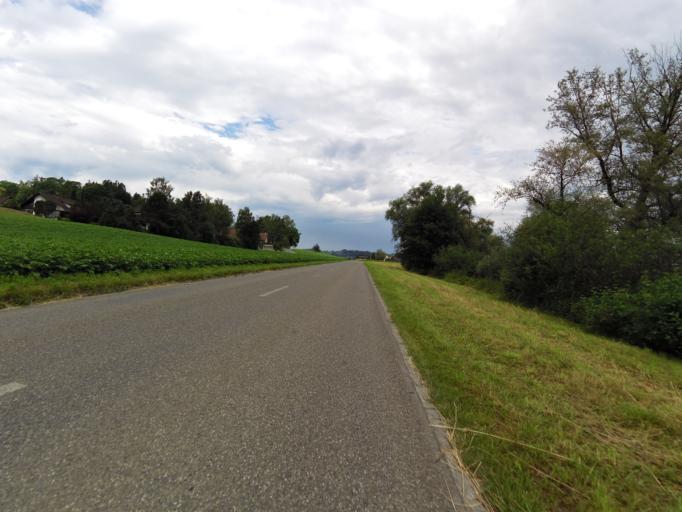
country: CH
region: Thurgau
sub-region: Frauenfeld District
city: Gachnang
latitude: 47.5574
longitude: 8.8609
